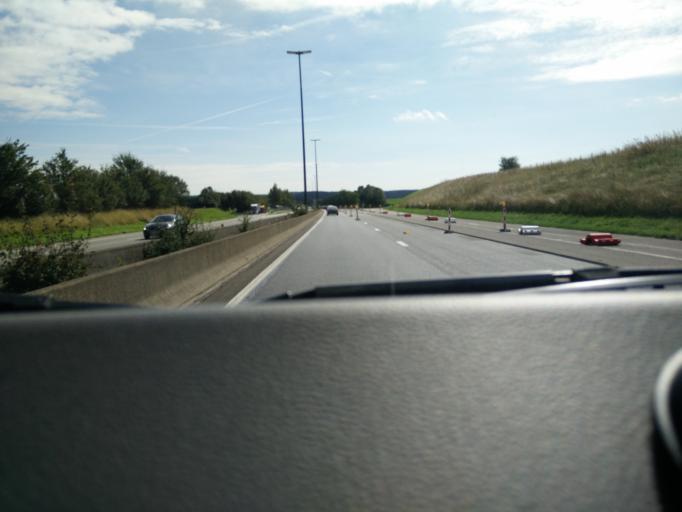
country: BE
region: Wallonia
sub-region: Province du Luxembourg
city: Neufchateau
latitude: 49.8906
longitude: 5.3523
